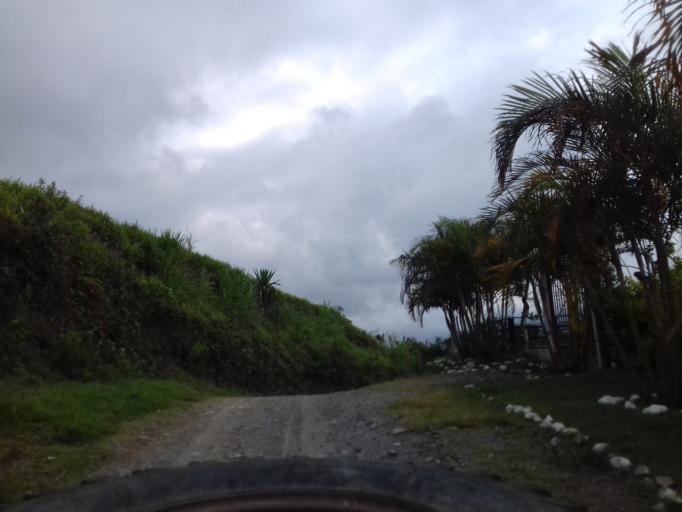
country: CO
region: Tolima
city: Libano
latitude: 4.9397
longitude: -75.0620
